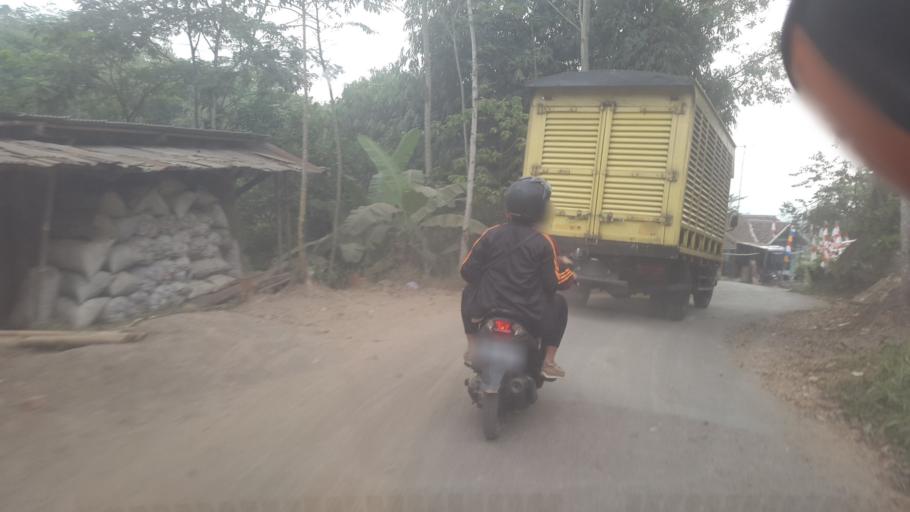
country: ID
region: West Java
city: Legok
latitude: -6.9914
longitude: 106.9472
